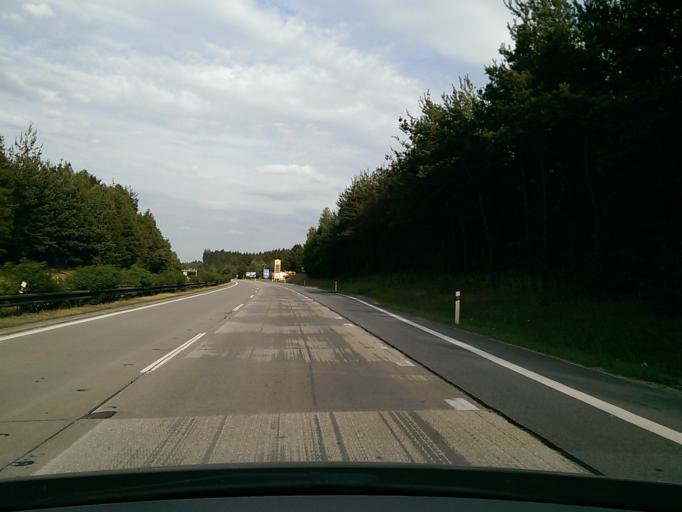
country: CZ
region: Vysocina
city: Luka nad Jihlavou
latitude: 49.4130
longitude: 15.7158
